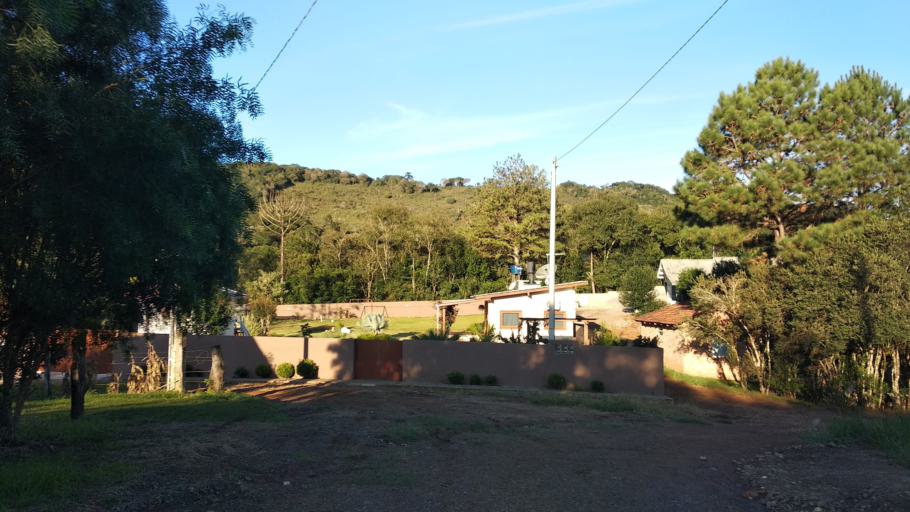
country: BR
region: Santa Catarina
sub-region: Celso Ramos
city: Celso Ramos
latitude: -27.5640
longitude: -51.2350
